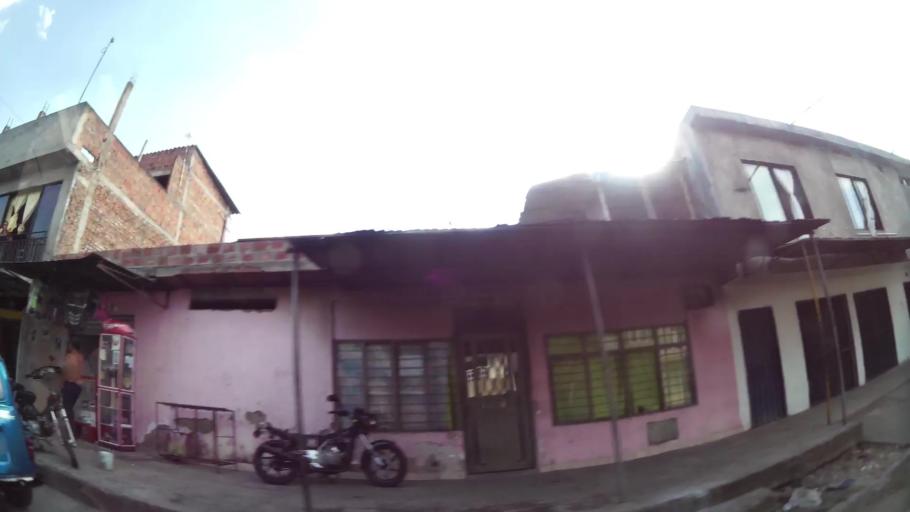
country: CO
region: Valle del Cauca
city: Cali
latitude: 3.4184
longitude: -76.4999
